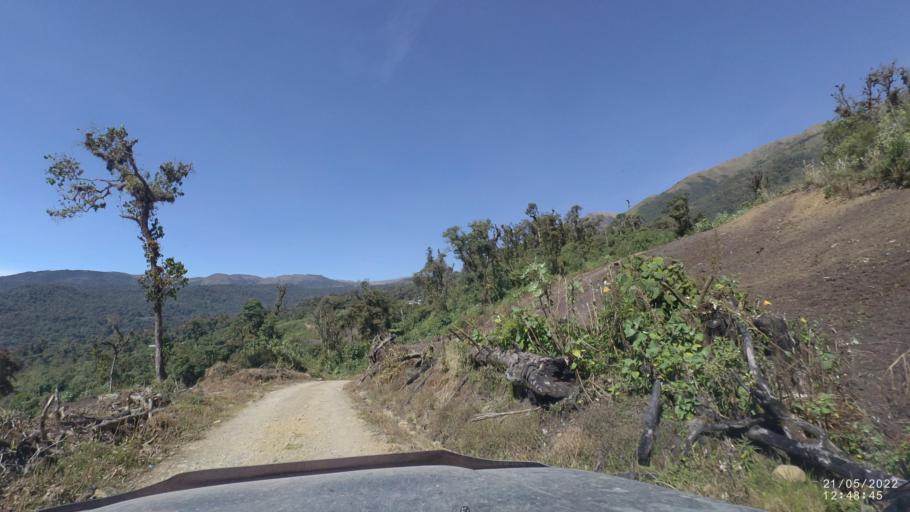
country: BO
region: Cochabamba
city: Colomi
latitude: -17.1795
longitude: -65.9426
